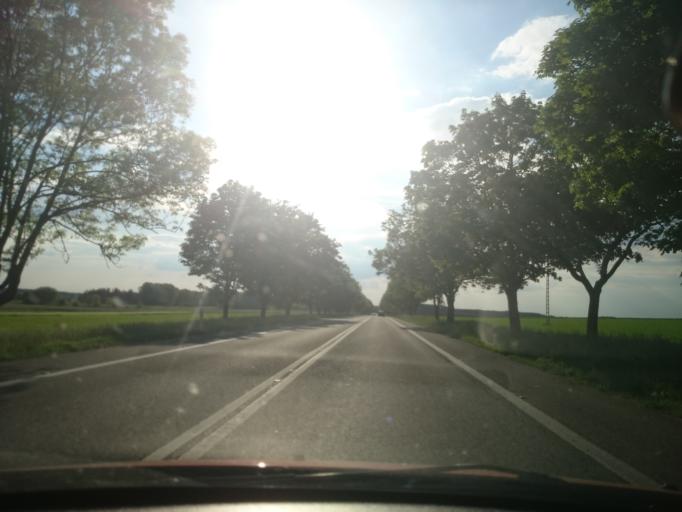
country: PL
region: Opole Voivodeship
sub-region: Powiat strzelecki
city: Izbicko
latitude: 50.5599
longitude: 18.1925
